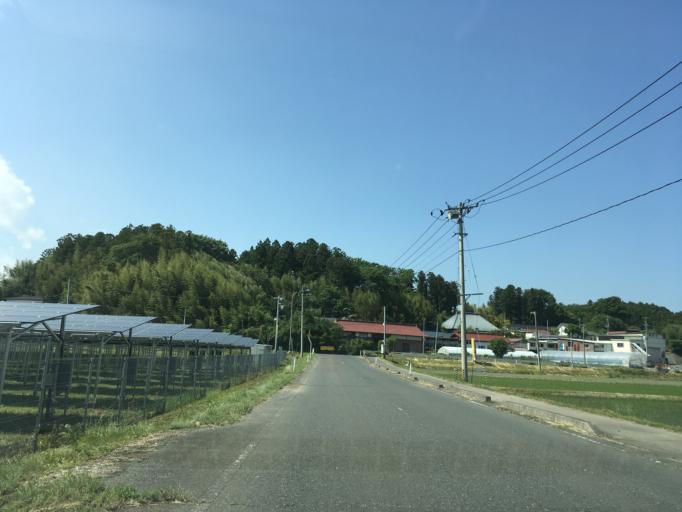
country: JP
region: Miyagi
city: Wakuya
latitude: 38.6671
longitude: 141.1577
